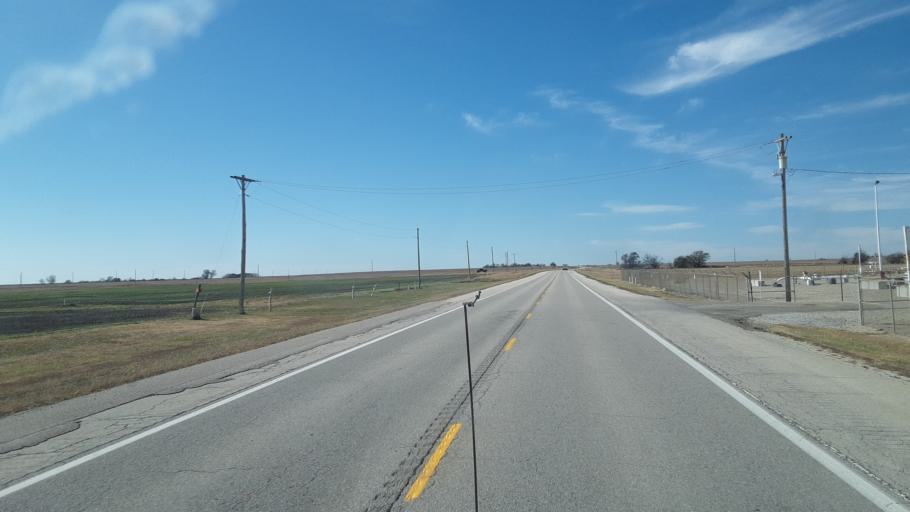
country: US
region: Kansas
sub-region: McPherson County
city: Inman
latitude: 38.3770
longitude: -97.8462
